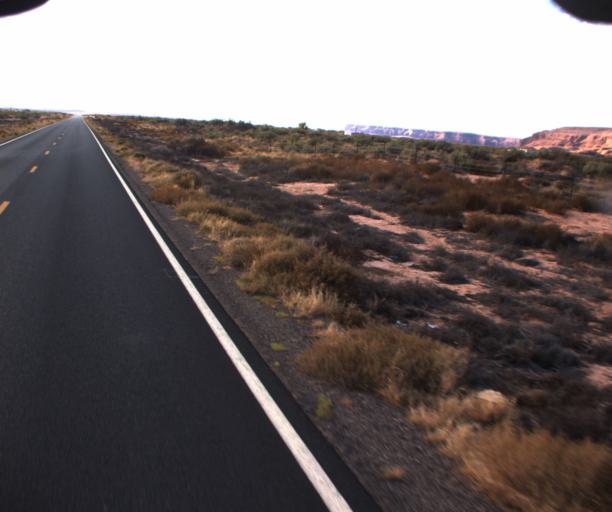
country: US
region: Arizona
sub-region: Apache County
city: Many Farms
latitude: 36.6582
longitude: -109.5948
